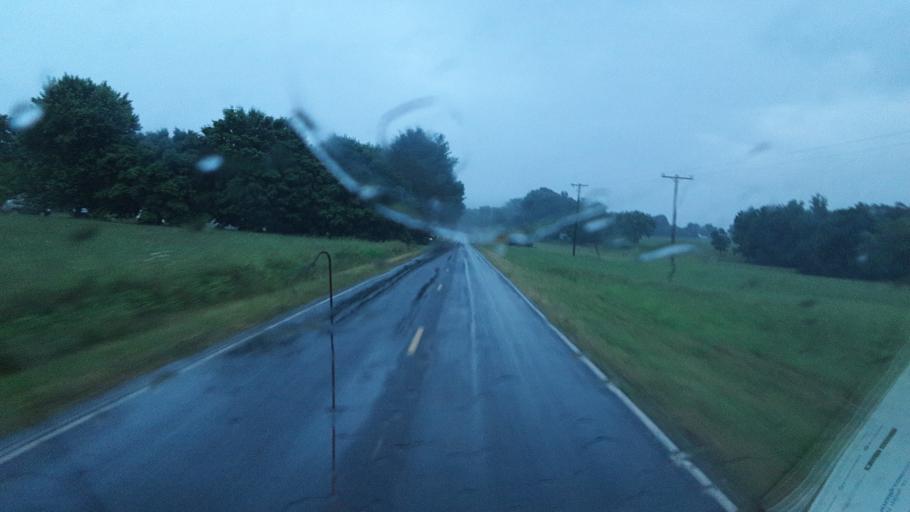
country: US
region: North Carolina
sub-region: Yadkin County
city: Jonesville
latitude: 36.0721
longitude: -80.8386
